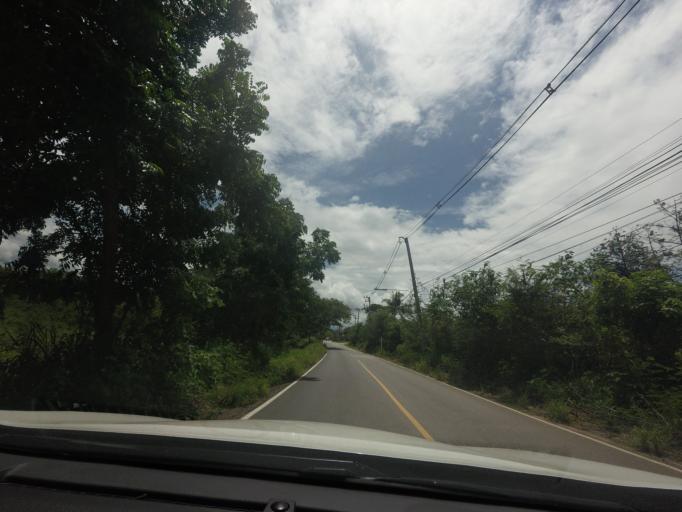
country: TH
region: Nakhon Ratchasima
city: Pak Chong
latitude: 14.5866
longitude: 101.4412
